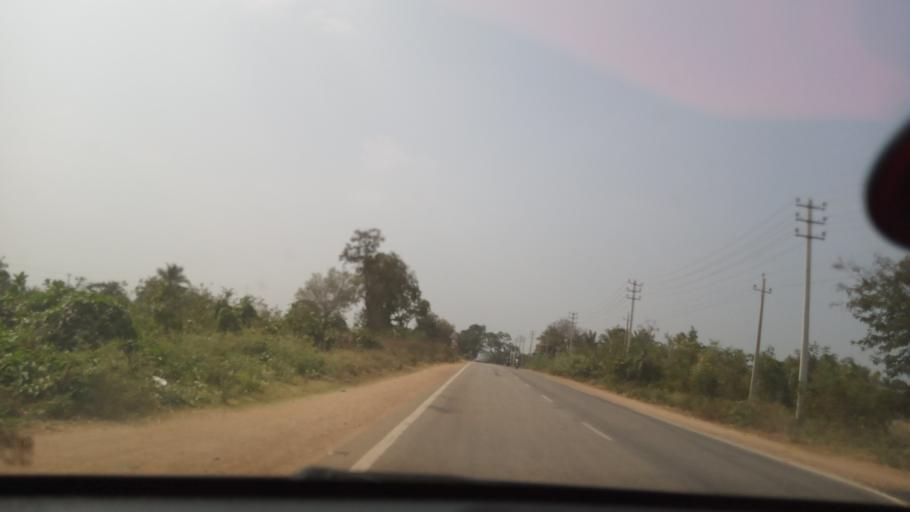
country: IN
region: Karnataka
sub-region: Chamrajnagar
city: Chamrajnagar
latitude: 11.9921
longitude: 76.8628
